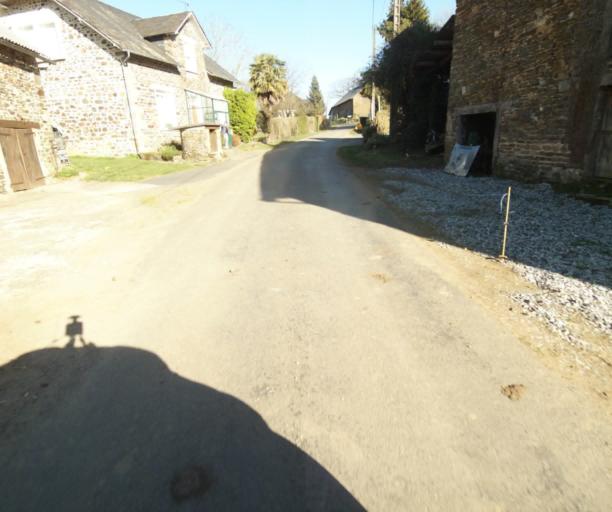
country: FR
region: Limousin
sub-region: Departement de la Correze
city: Seilhac
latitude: 45.3915
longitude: 1.6799
